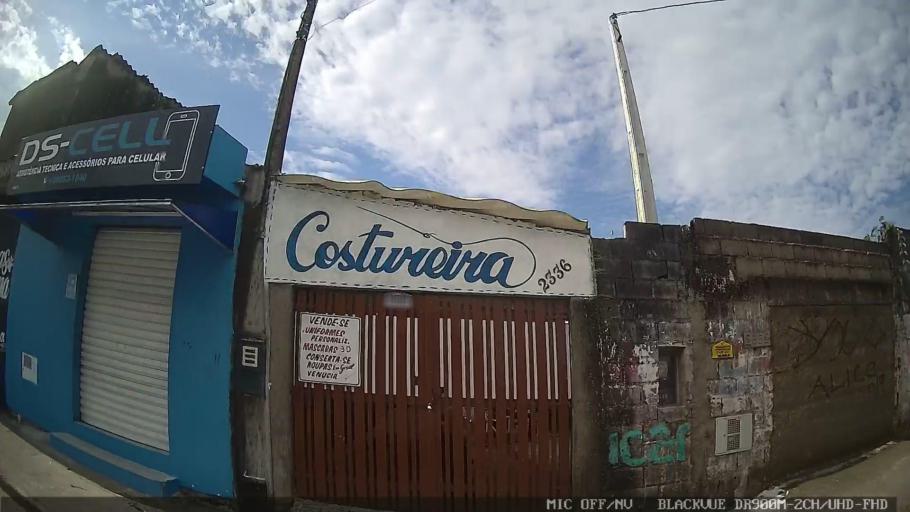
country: BR
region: Sao Paulo
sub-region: Itanhaem
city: Itanhaem
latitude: -24.1508
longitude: -46.7783
